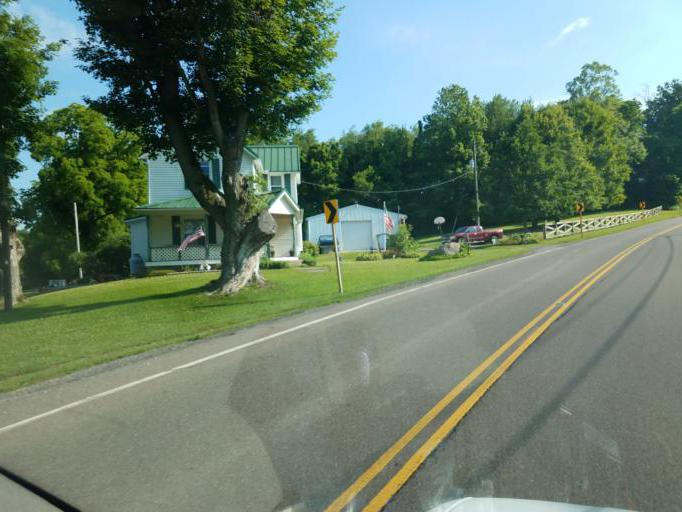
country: US
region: Ohio
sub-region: Knox County
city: Fredericktown
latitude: 40.4937
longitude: -82.5433
